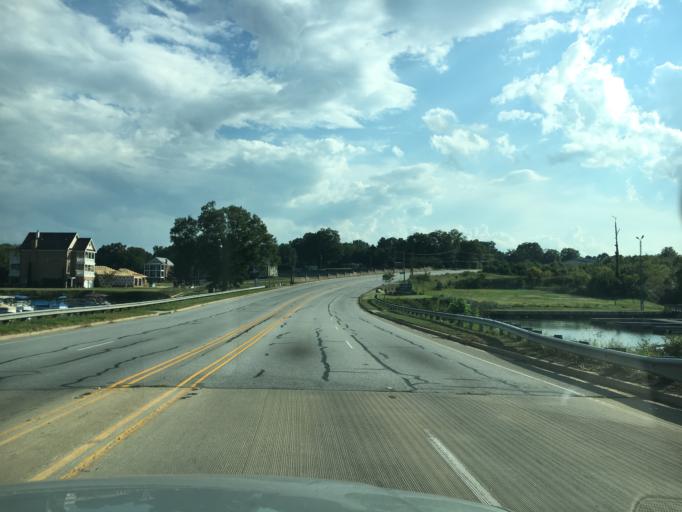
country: US
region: South Carolina
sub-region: Greenwood County
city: Ninety Six
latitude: 34.2788
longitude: -82.0590
